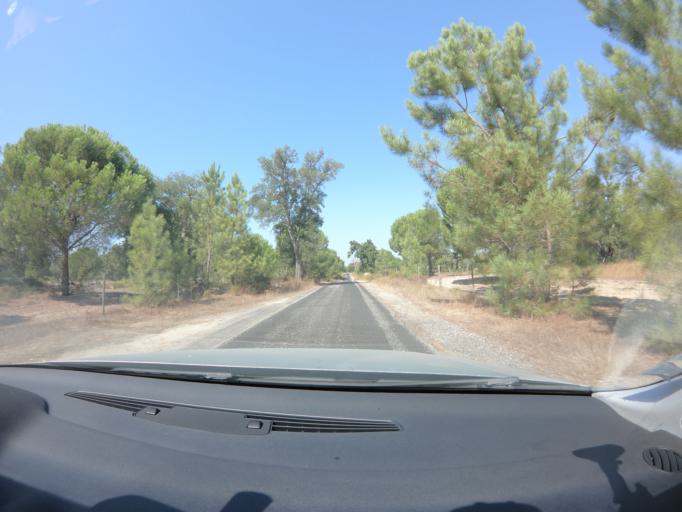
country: PT
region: Setubal
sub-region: Alcacer do Sal
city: Alcacer do Sal
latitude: 38.2614
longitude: -8.3095
